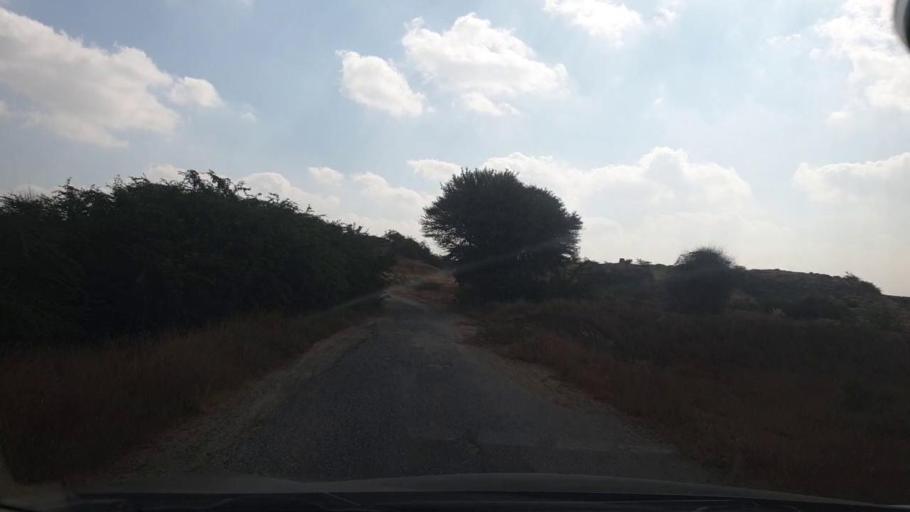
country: PK
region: Sindh
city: Malir Cantonment
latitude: 25.0251
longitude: 67.3500
